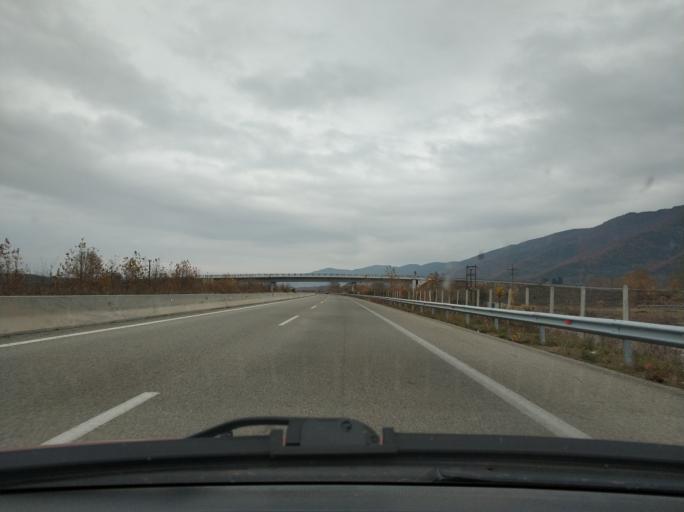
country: GR
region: East Macedonia and Thrace
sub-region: Nomos Kavalas
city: Eleftheres
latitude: 40.8662
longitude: 24.1901
